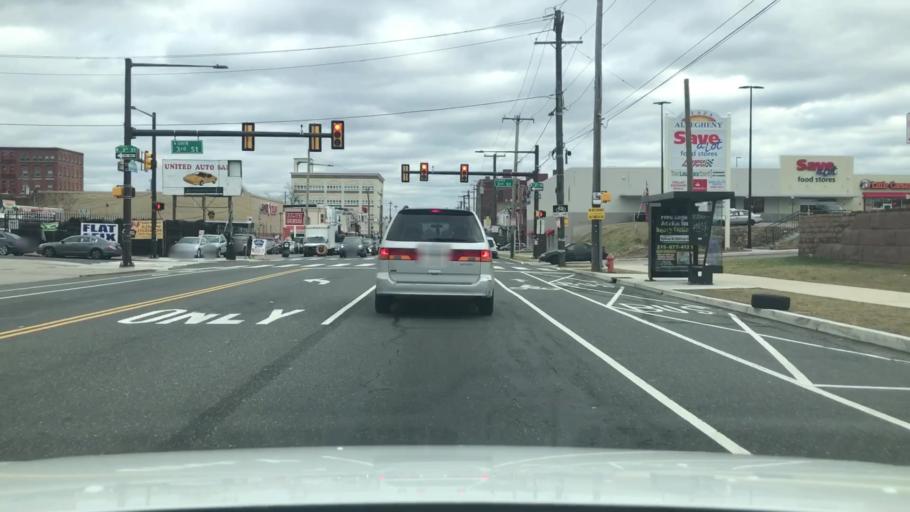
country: US
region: Pennsylvania
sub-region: Philadelphia County
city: Philadelphia
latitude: 39.9994
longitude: -75.1362
